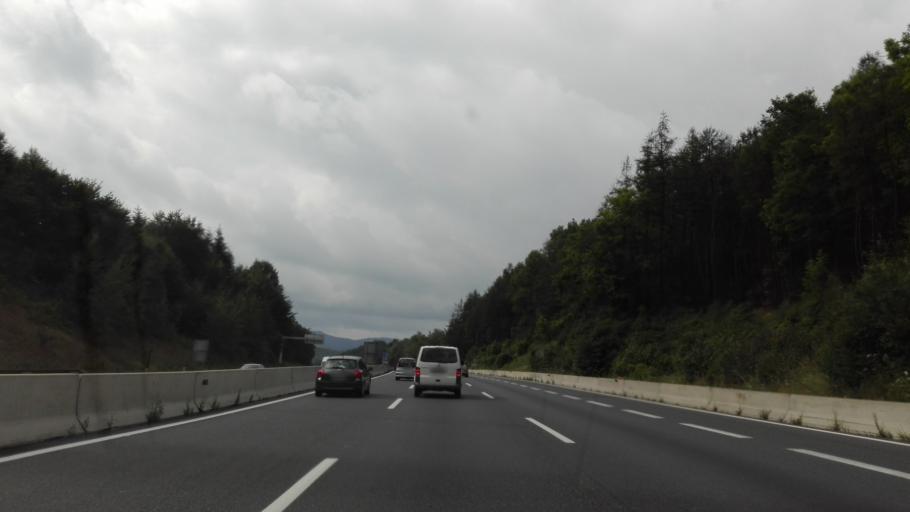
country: AT
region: Lower Austria
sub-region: Politischer Bezirk Sankt Polten
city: Eichgraben
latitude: 48.1316
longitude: 15.9717
